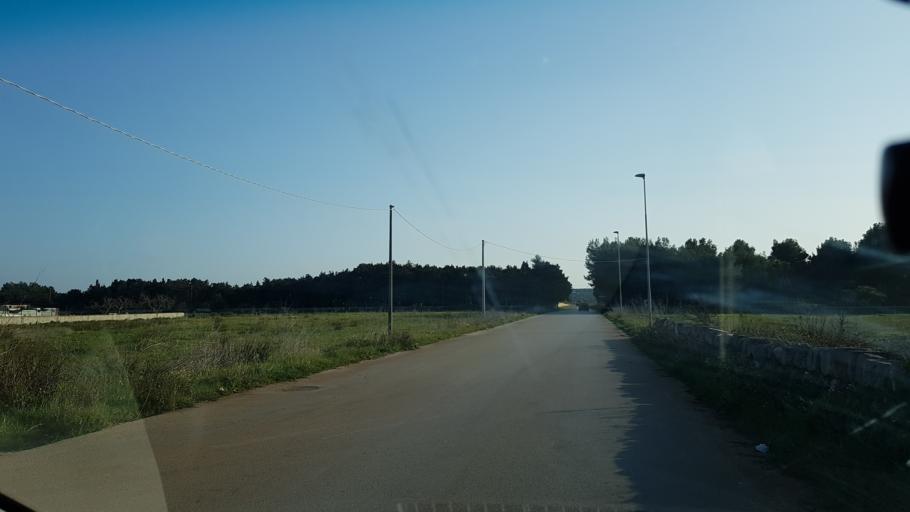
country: IT
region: Apulia
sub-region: Provincia di Brindisi
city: Carovigno
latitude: 40.7423
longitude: 17.7290
